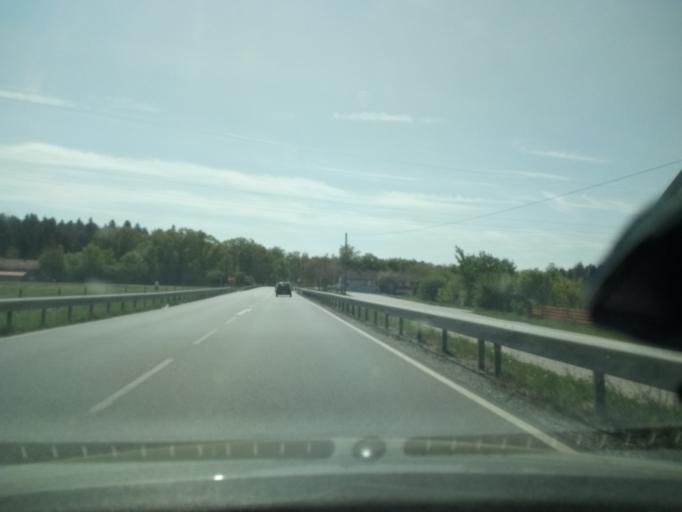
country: DE
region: Bavaria
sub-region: Upper Bavaria
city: Ampfing
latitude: 48.2352
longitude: 12.4135
